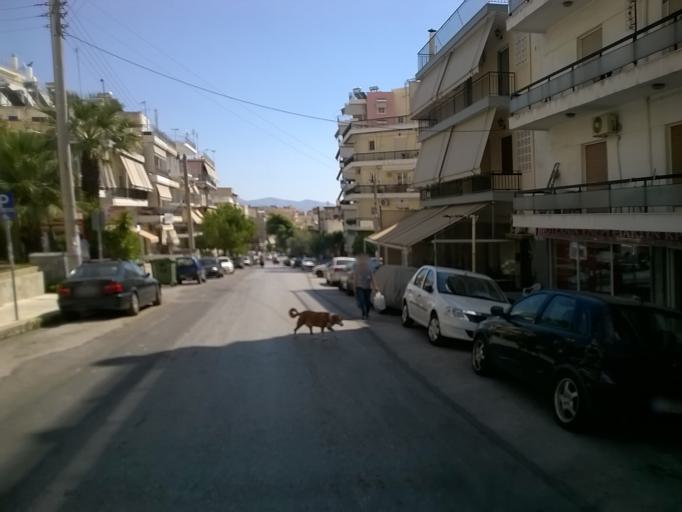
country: GR
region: Attica
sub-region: Nomos Piraios
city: Keratsini
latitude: 37.9689
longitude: 23.6160
